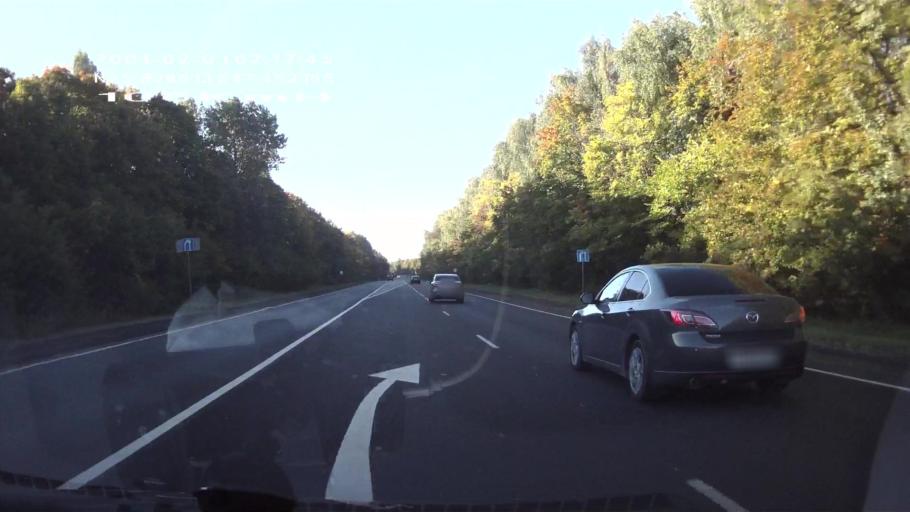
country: RU
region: Chuvashia
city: Tsivil'sk
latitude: 55.8281
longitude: 47.4514
